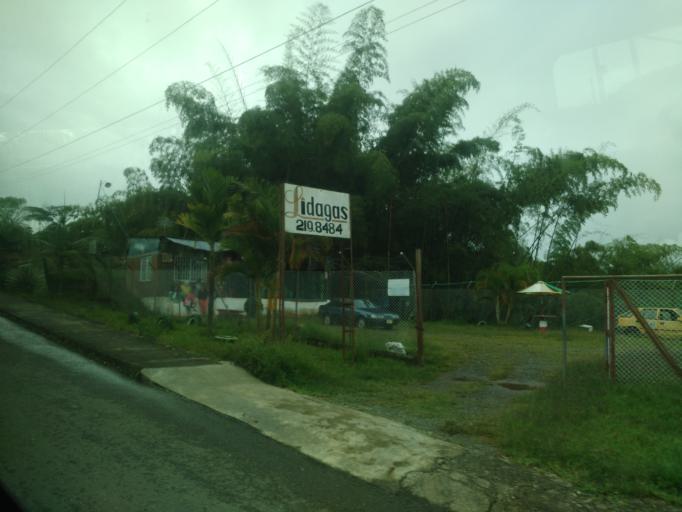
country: CO
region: Valle del Cauca
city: Sevilla
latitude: 4.2684
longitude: -75.9238
